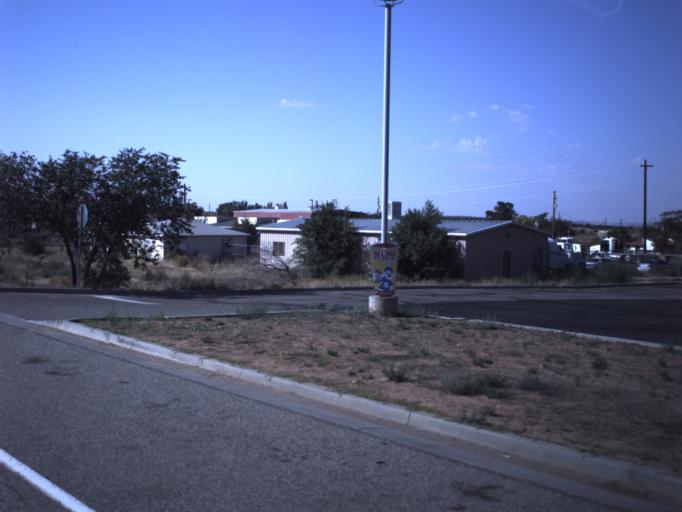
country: US
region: Utah
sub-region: San Juan County
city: Blanding
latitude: 37.4654
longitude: -109.4670
